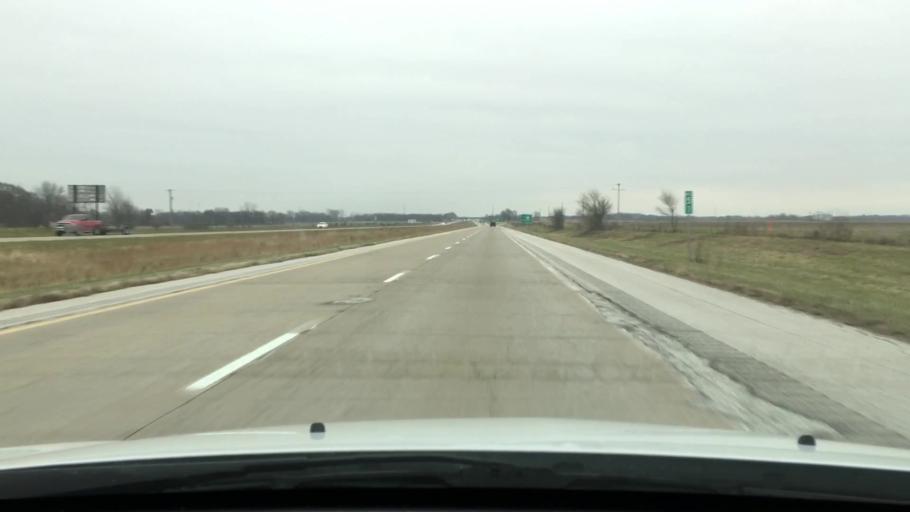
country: US
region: Illinois
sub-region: Scott County
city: Winchester
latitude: 39.6809
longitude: -90.4754
